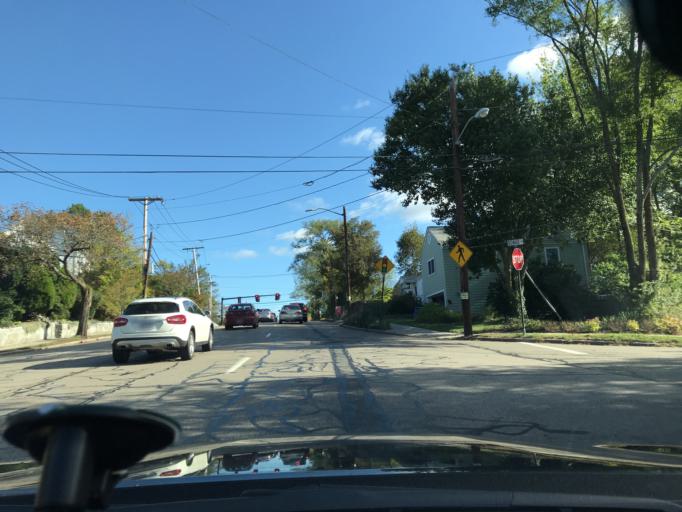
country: US
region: Massachusetts
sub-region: Suffolk County
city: Jamaica Plain
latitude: 42.3016
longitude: -71.1533
